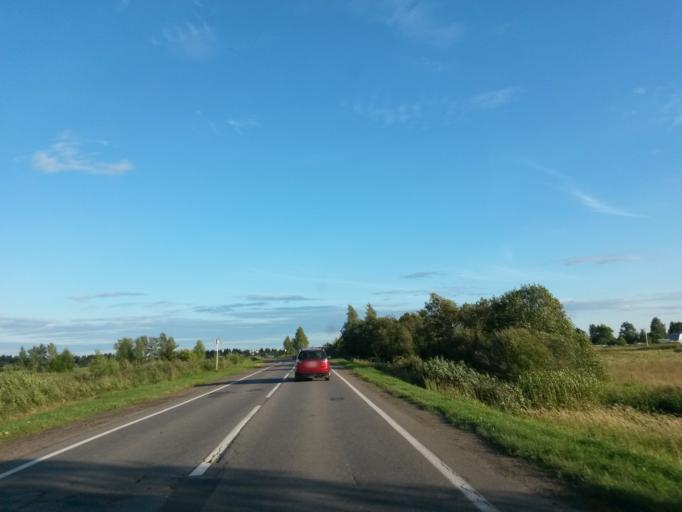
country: RU
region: Jaroslavl
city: Yaroslavl
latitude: 57.7927
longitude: 39.8293
